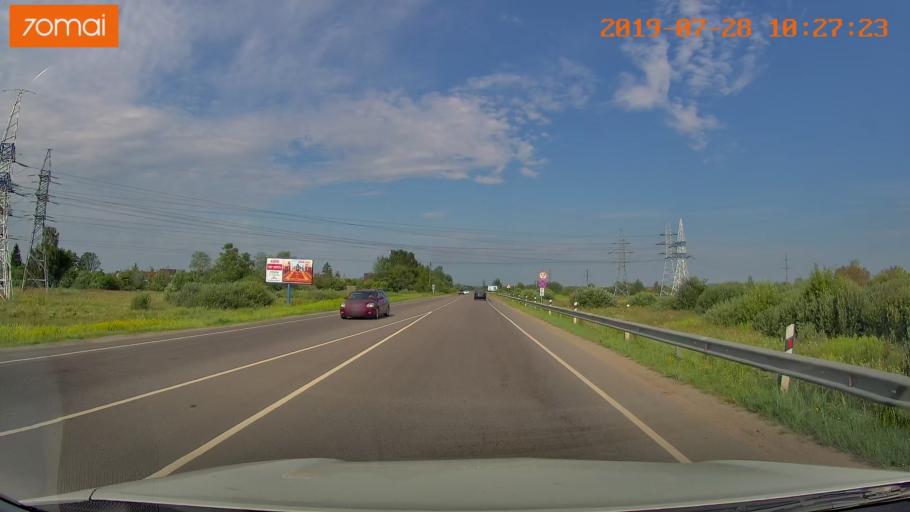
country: RU
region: Kaliningrad
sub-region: Gorod Kaliningrad
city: Kaliningrad
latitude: 54.7705
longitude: 20.5185
